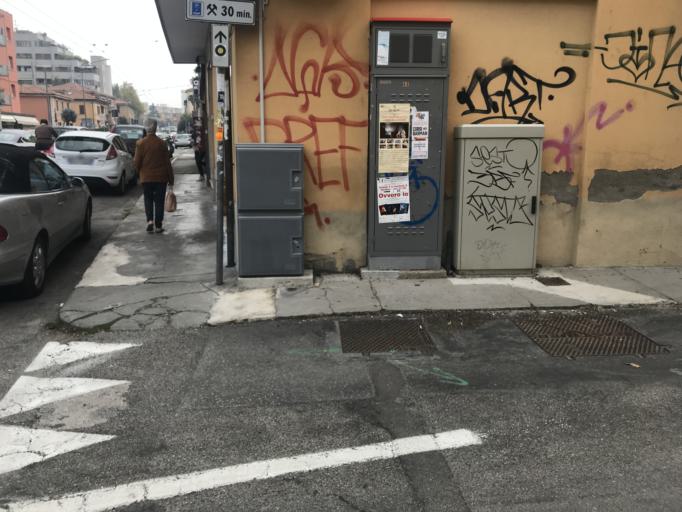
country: IT
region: Emilia-Romagna
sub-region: Provincia di Bologna
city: Ponticella
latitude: 44.4934
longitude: 11.3840
